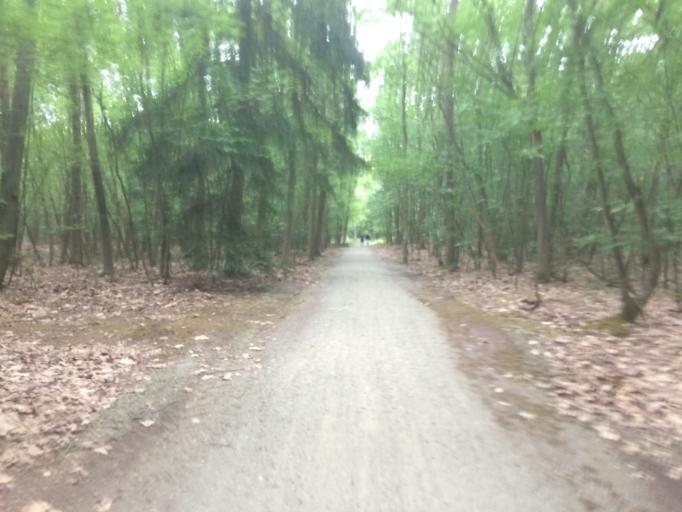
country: DK
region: Capital Region
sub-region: Bornholm Kommune
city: Ronne
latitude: 55.1285
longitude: 14.7141
